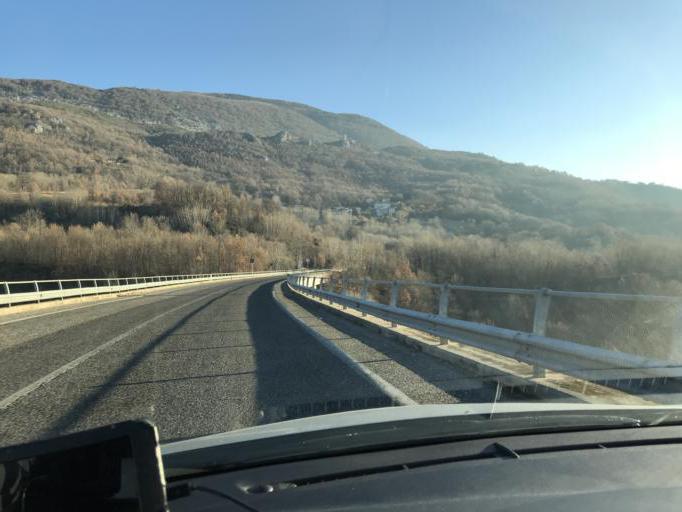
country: IT
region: Latium
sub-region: Provincia di Rieti
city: Fiamignano
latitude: 42.2632
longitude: 13.1014
